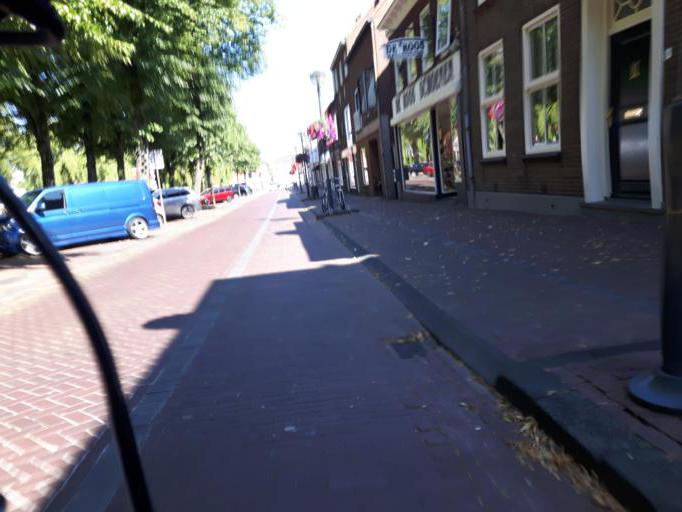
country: NL
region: North Brabant
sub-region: Gemeente Moerdijk
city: Klundert
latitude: 51.6632
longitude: 4.5347
